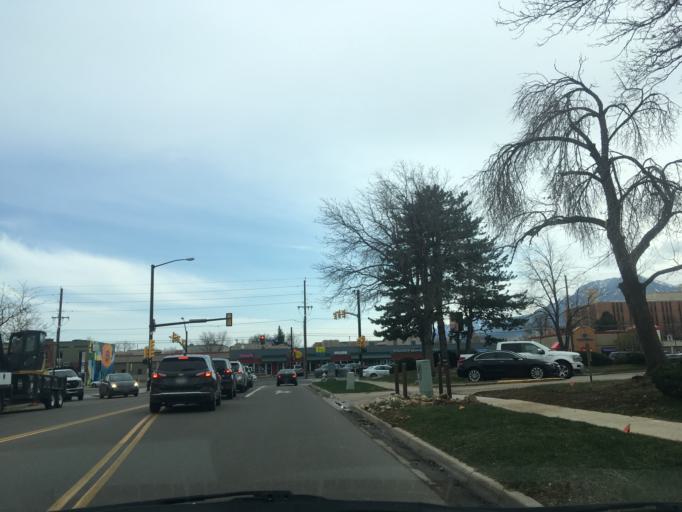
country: US
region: Colorado
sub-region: Boulder County
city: Boulder
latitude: 40.0153
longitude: -105.2502
